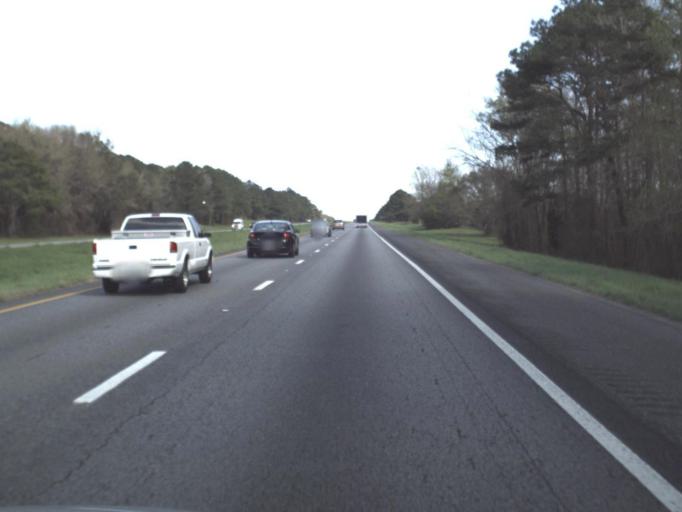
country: US
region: Florida
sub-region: Leon County
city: Tallahassee
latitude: 30.4781
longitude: -84.1230
